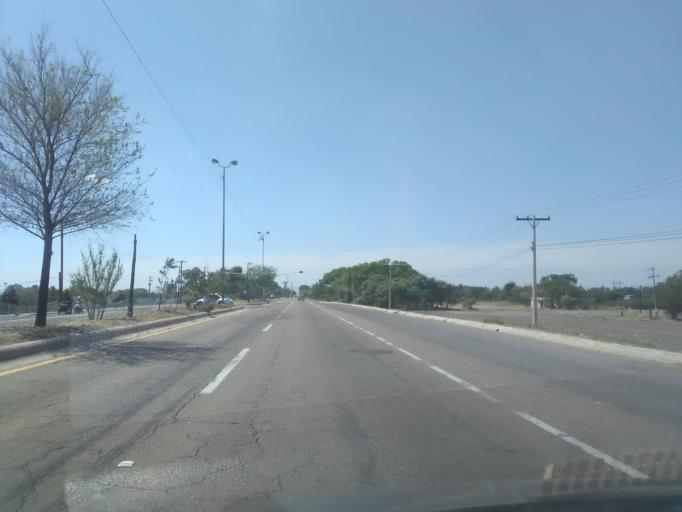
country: MX
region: Durango
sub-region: Durango
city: Jose Refugio Salcido
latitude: 24.0242
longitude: -104.5542
